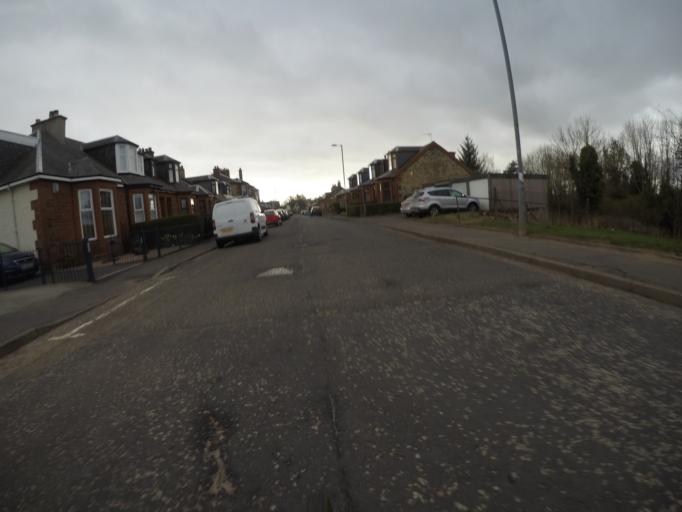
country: GB
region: Scotland
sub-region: East Ayrshire
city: Kilmarnock
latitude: 55.6166
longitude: -4.4858
